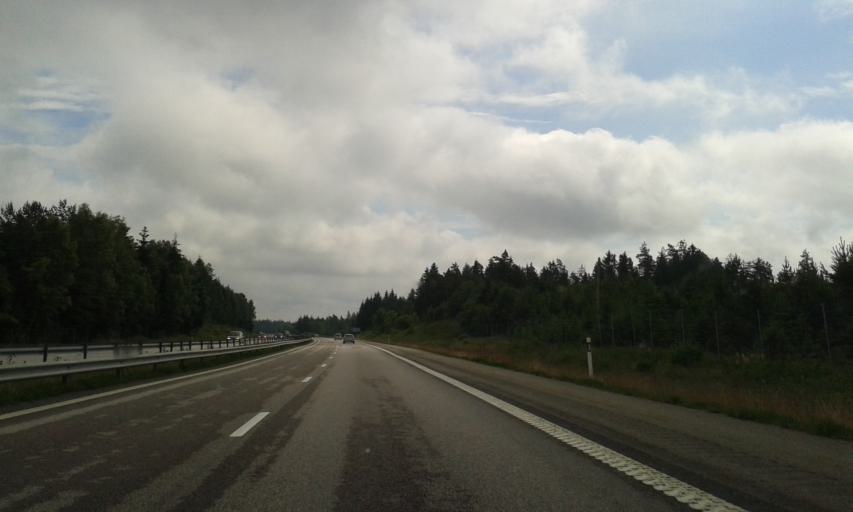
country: SE
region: Vaestra Goetaland
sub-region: Boras Kommun
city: Sandared
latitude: 57.6809
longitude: 12.7282
